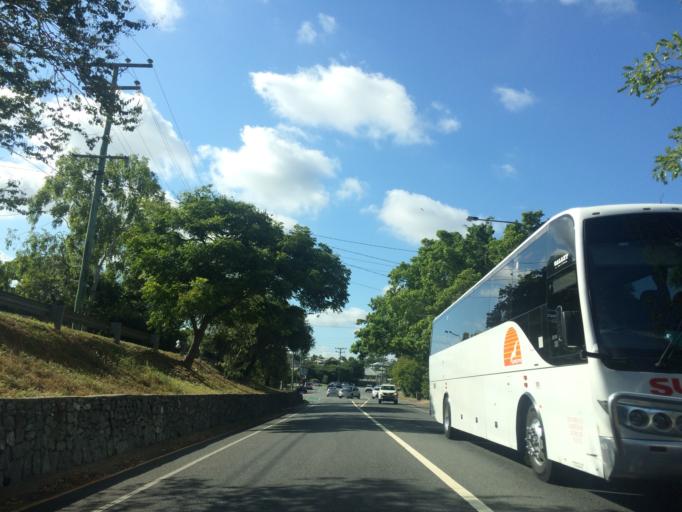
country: AU
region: Queensland
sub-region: Brisbane
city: Seven Hills
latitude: -27.4796
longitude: 153.0645
